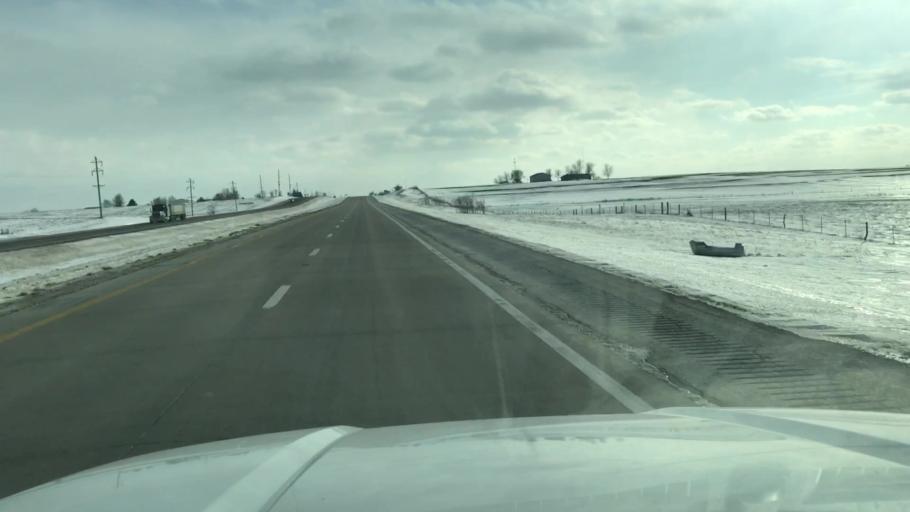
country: US
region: Missouri
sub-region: Nodaway County
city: Maryville
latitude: 40.2655
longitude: -94.8670
